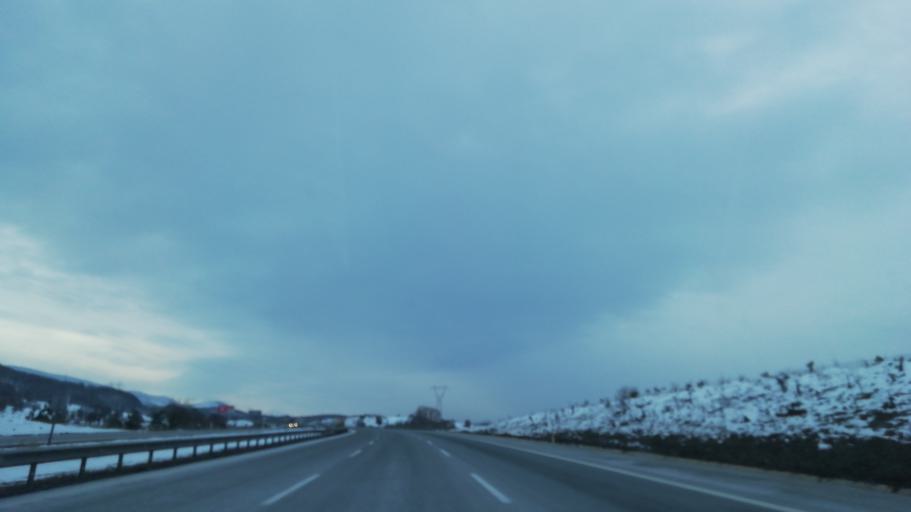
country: TR
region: Bolu
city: Yenicaga
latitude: 40.7619
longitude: 31.9828
